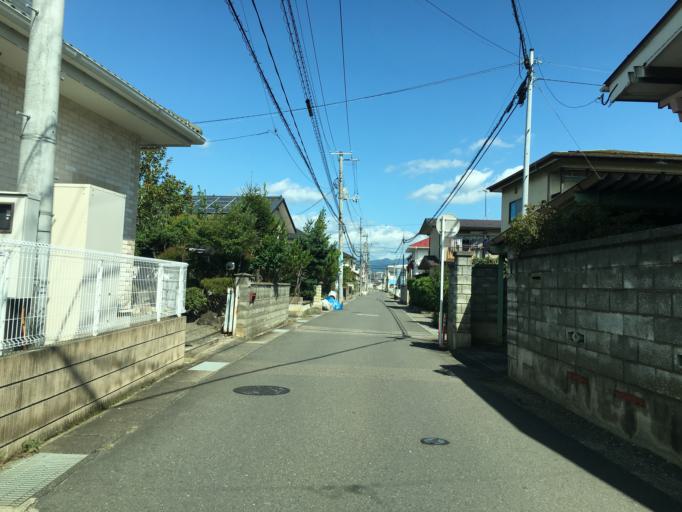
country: JP
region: Fukushima
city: Fukushima-shi
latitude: 37.7425
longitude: 140.4505
